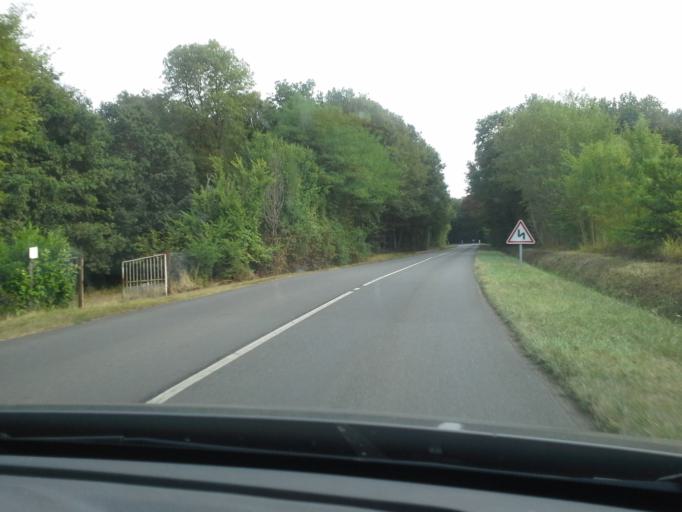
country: FR
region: Centre
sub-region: Departement du Loir-et-Cher
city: Herbault
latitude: 47.5866
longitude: 1.2019
